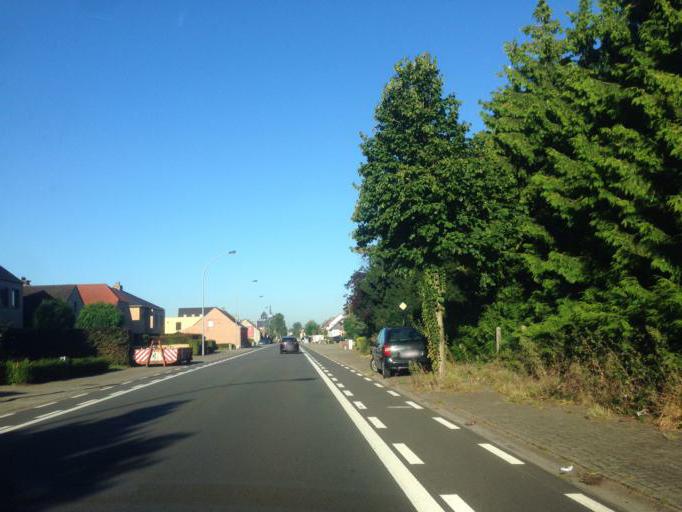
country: BE
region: Flanders
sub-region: Provincie Antwerpen
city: Geel
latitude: 51.1637
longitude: 5.0146
